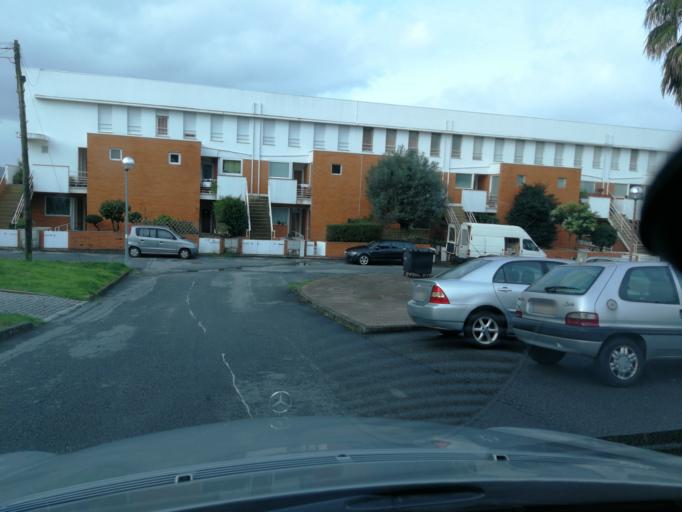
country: PT
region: Braga
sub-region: Braga
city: Braga
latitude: 41.5319
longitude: -8.4144
